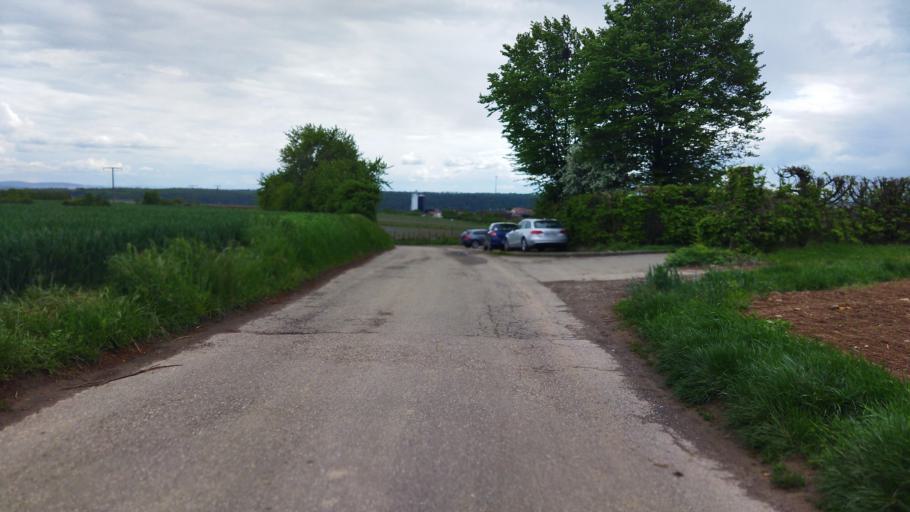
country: DE
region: Baden-Wuerttemberg
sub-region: Regierungsbezirk Stuttgart
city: Hessigheim
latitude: 49.0117
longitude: 9.1885
